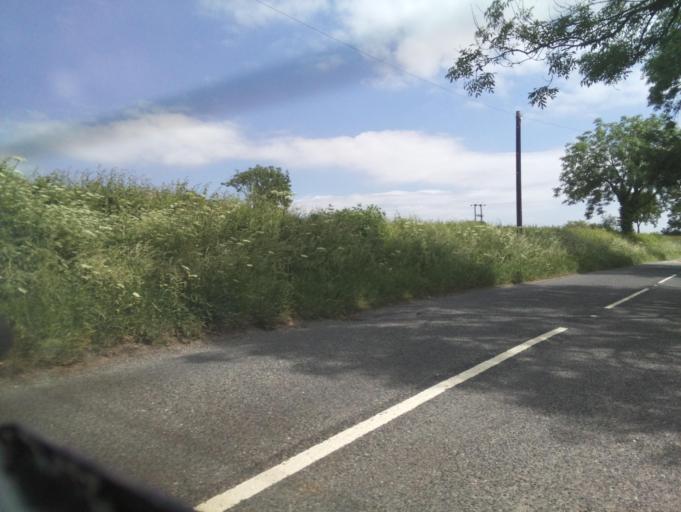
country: GB
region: England
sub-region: Somerset
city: Wincanton
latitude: 51.0314
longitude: -2.4525
